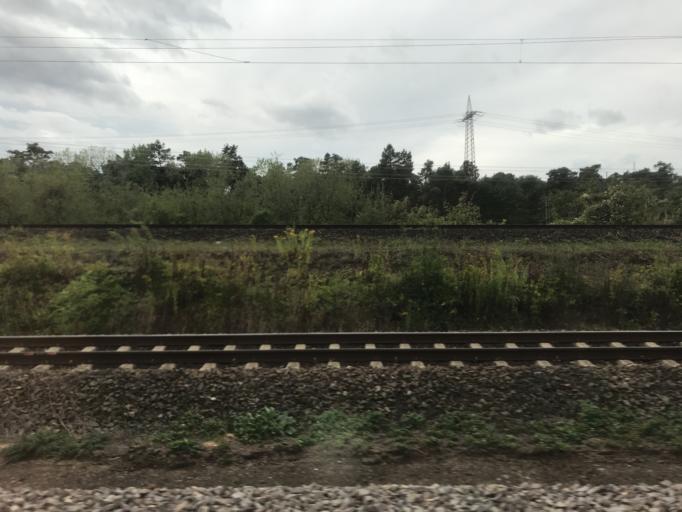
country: DE
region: Baden-Wuerttemberg
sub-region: Karlsruhe Region
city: Ilvesheim
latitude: 49.4456
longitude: 8.5524
